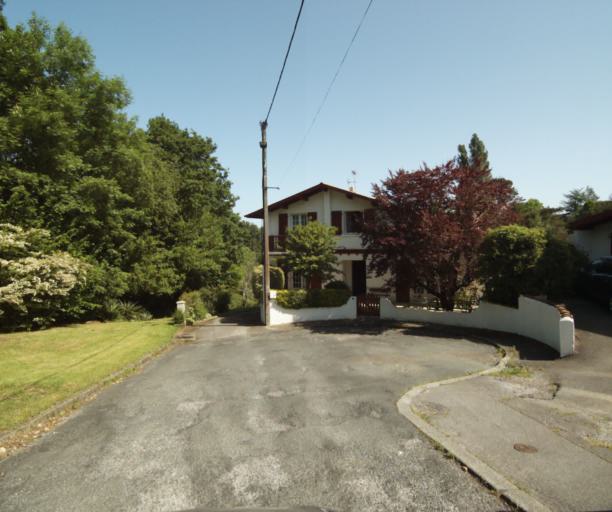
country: FR
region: Aquitaine
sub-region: Departement des Pyrenees-Atlantiques
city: Mouguerre
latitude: 43.4741
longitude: -1.4497
